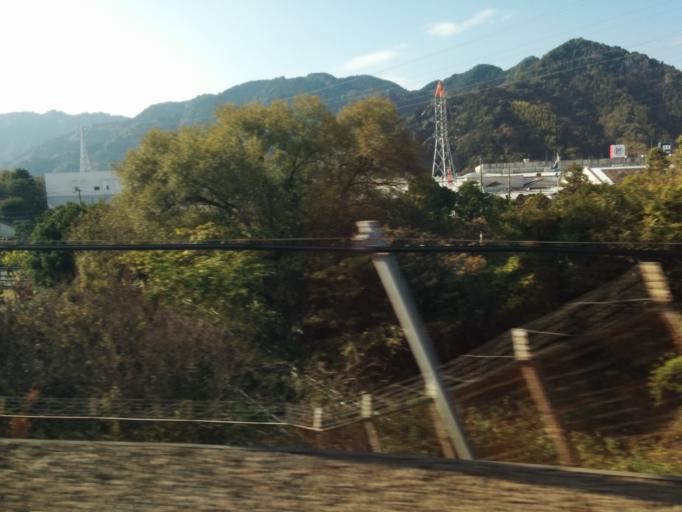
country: JP
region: Shizuoka
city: Shizuoka-shi
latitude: 34.9301
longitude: 138.3626
